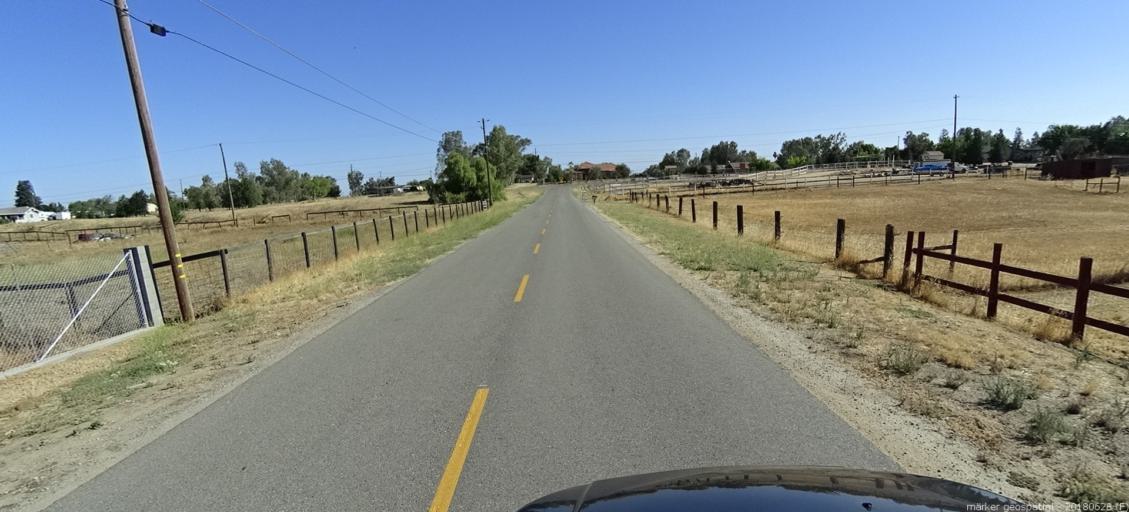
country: US
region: California
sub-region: Madera County
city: Bonadelle Ranchos-Madera Ranchos
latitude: 37.0015
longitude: -119.8901
